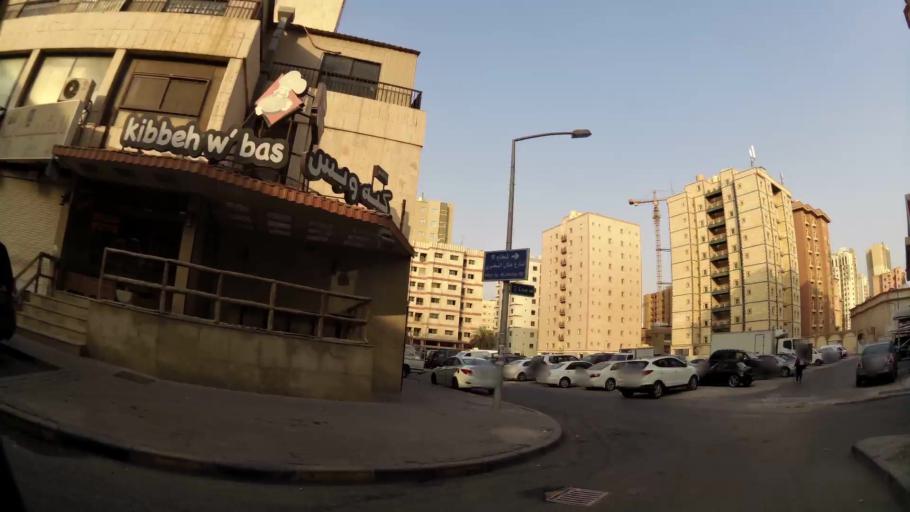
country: KW
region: Muhafazat Hawalli
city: As Salimiyah
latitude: 29.3340
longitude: 48.0573
